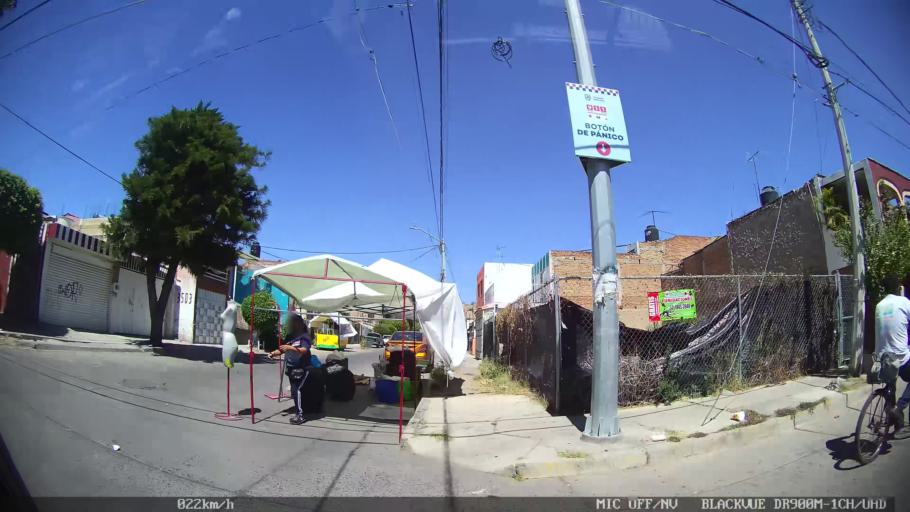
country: MX
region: Jalisco
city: Tlaquepaque
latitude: 20.6635
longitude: -103.2853
